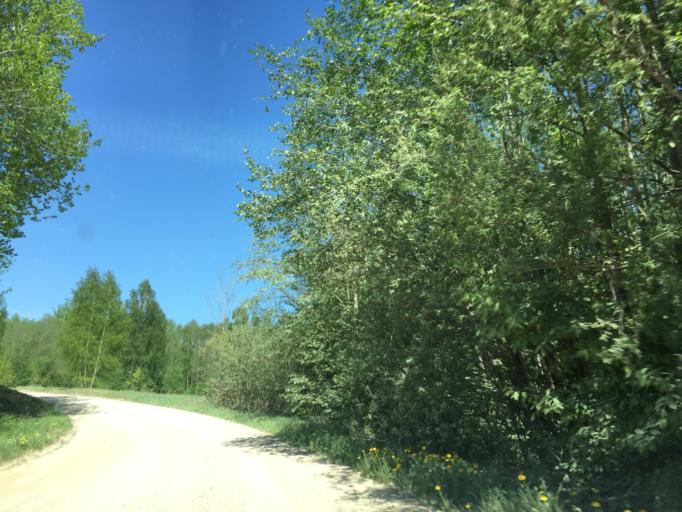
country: LV
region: Ikskile
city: Ikskile
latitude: 56.8709
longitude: 24.5020
